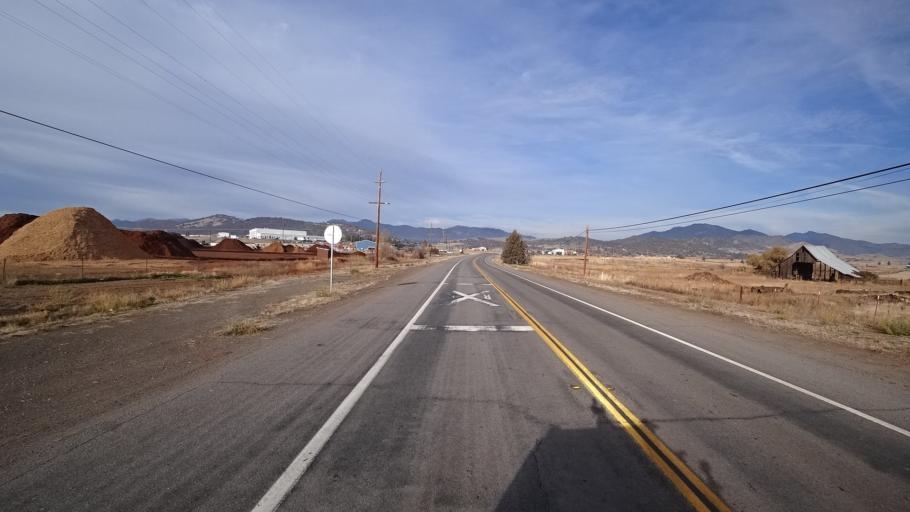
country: US
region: California
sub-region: Siskiyou County
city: Yreka
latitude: 41.7341
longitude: -122.5902
